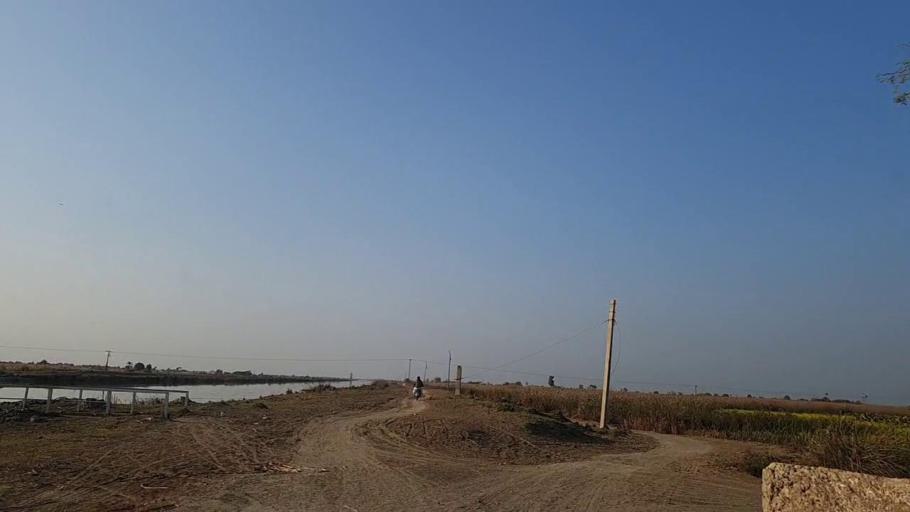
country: PK
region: Sindh
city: Sakrand
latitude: 26.0947
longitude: 68.3722
